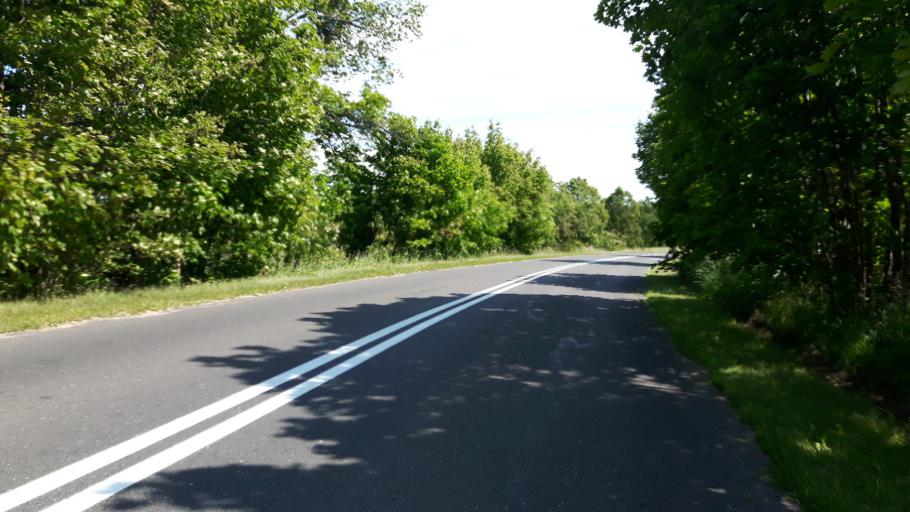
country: PL
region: Pomeranian Voivodeship
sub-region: Powiat wejherowski
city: Gniewino
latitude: 54.7056
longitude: 18.0608
